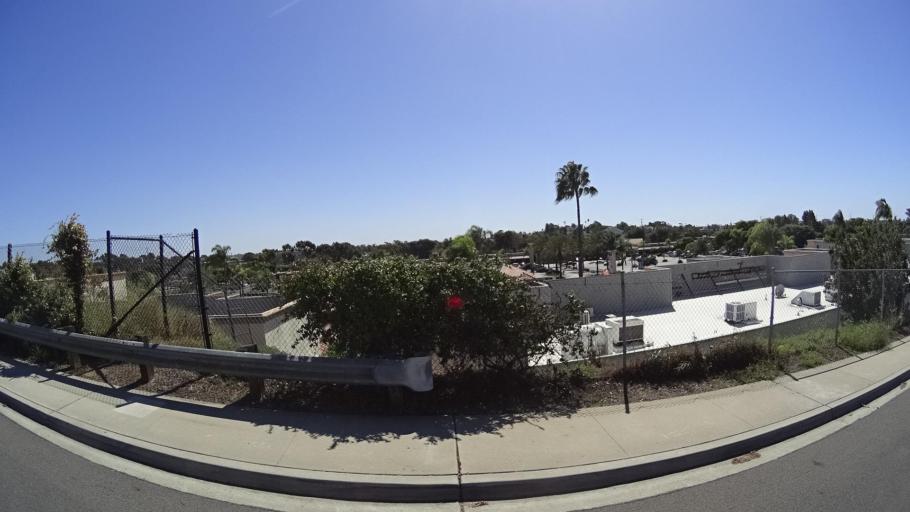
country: US
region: California
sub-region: San Diego County
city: Chula Vista
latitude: 32.6624
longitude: -117.0824
